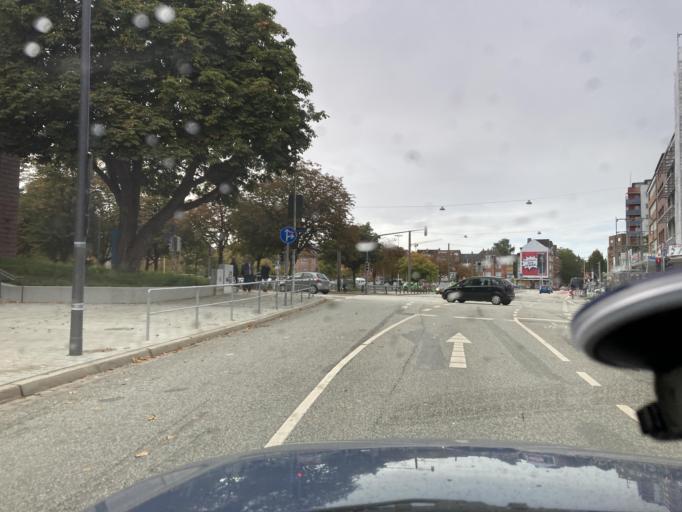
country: DE
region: Schleswig-Holstein
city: Kiel
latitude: 54.3214
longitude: 10.1300
